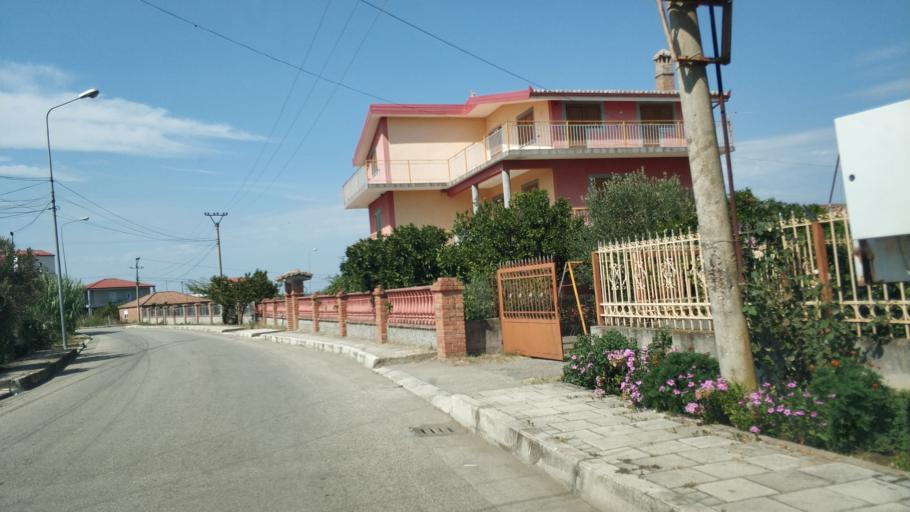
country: AL
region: Fier
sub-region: Rrethi i Lushnjes
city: Divjake
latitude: 40.9989
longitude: 19.5266
